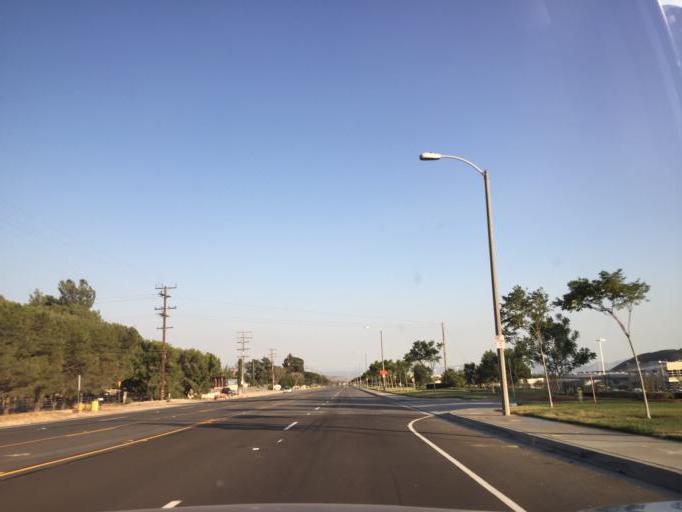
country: US
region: California
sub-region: San Bernardino County
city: Muscoy
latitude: 34.2189
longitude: -117.4005
